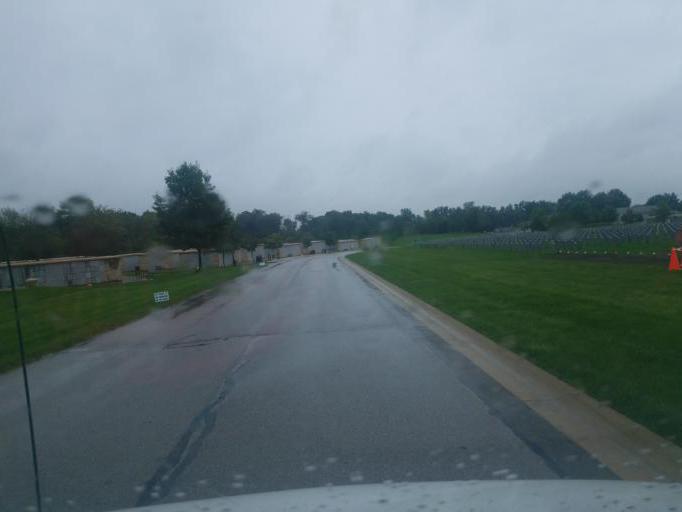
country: US
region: Ohio
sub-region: Wayne County
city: Rittman
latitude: 40.9994
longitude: -81.8112
